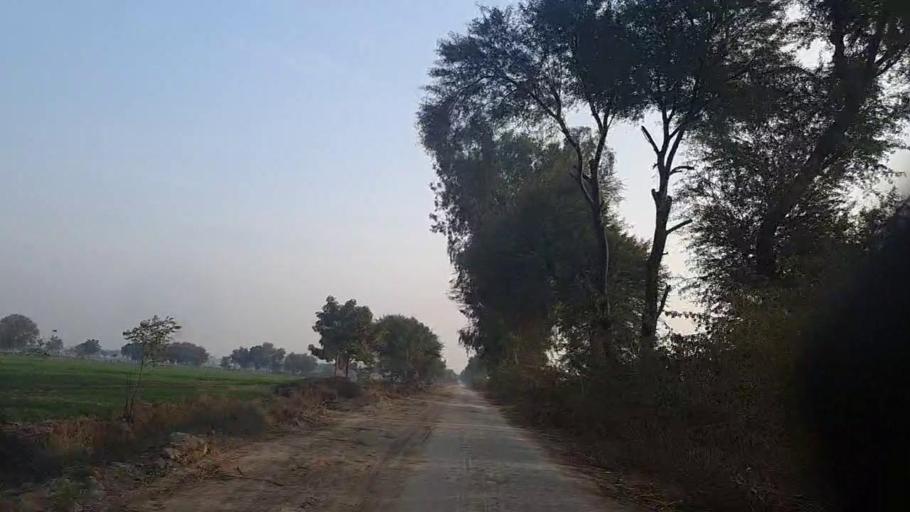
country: PK
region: Sindh
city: Sakrand
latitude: 26.1265
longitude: 68.2298
